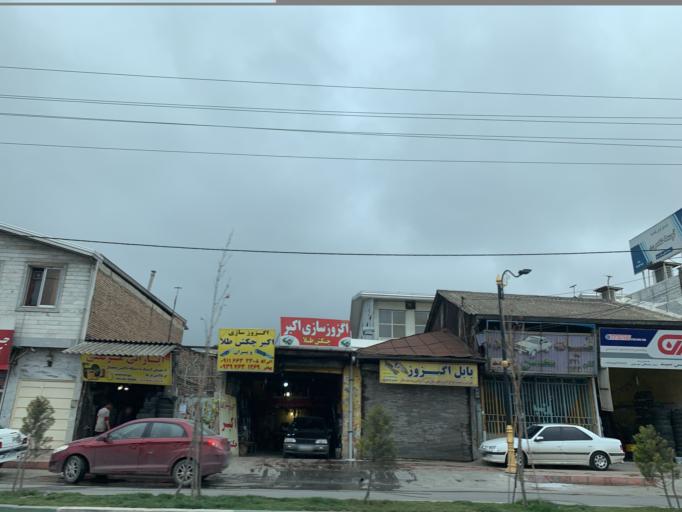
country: IR
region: Mazandaran
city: Babol
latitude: 36.5346
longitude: 52.6524
